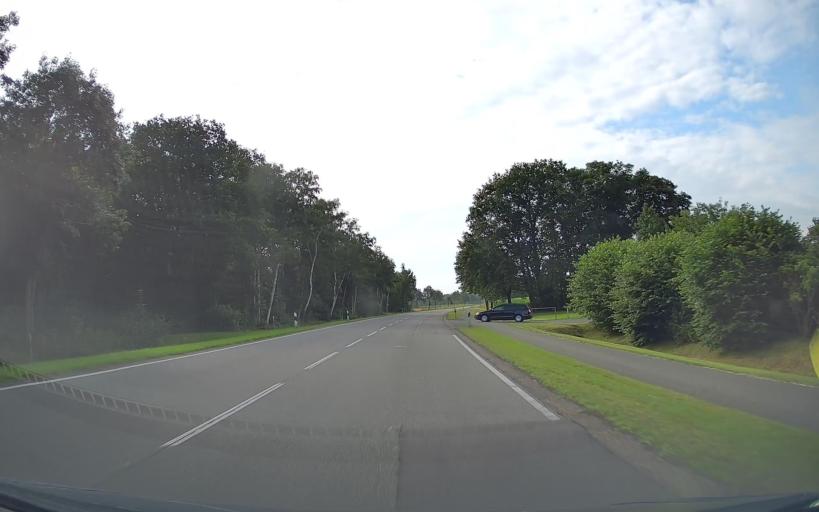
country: DE
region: Lower Saxony
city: Friesoythe
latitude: 52.9858
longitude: 7.8933
